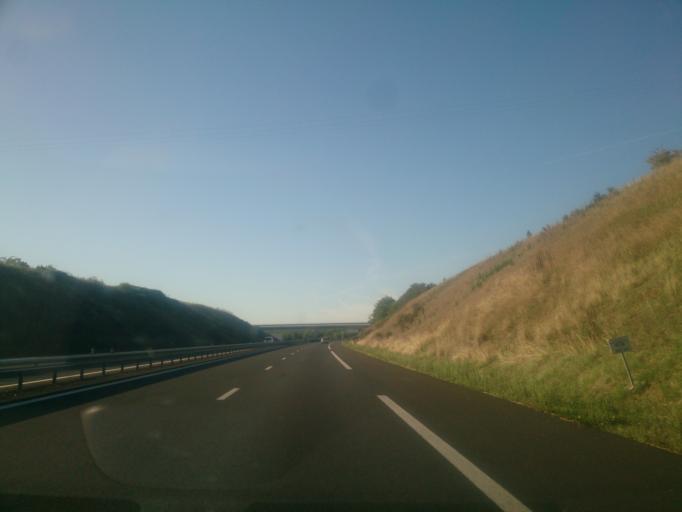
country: FR
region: Midi-Pyrenees
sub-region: Departement du Lot
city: Cahors
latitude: 44.5611
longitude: 1.5144
